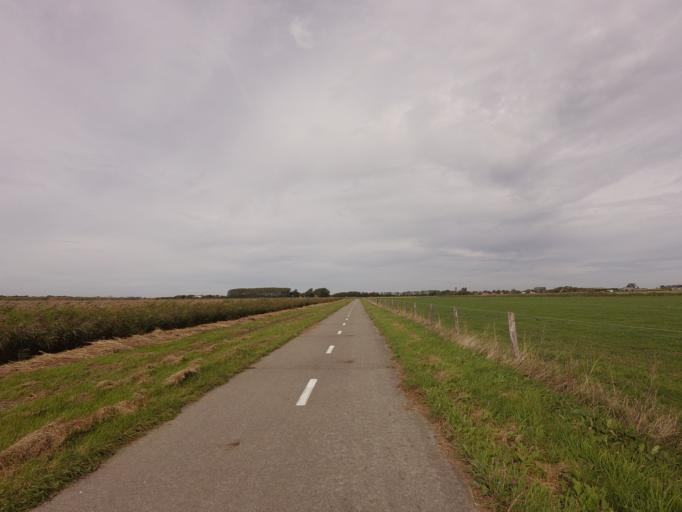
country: NL
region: North Holland
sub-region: Gemeente Texel
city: Den Burg
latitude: 53.0630
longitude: 4.8232
